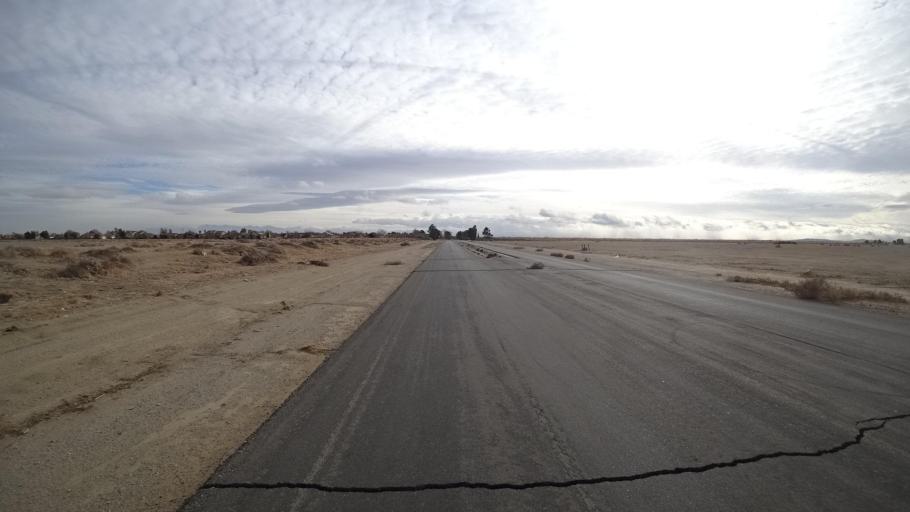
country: US
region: California
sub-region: Kern County
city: Rosamond
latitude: 34.8588
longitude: -118.2024
